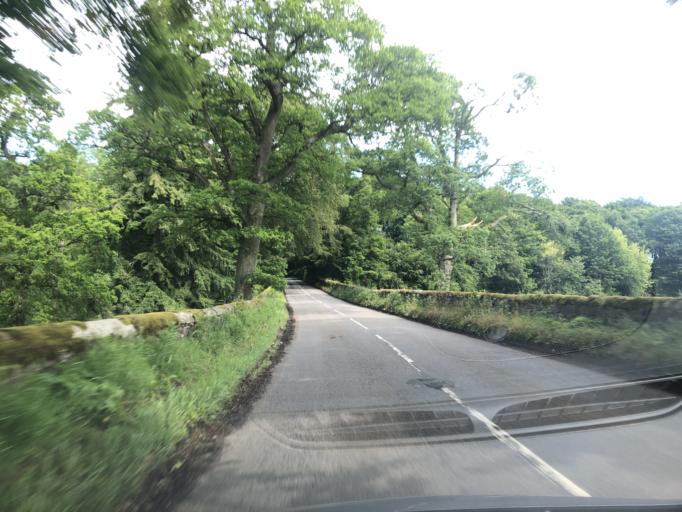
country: GB
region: Scotland
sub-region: Angus
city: Kirriemuir
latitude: 56.7162
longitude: -2.9888
